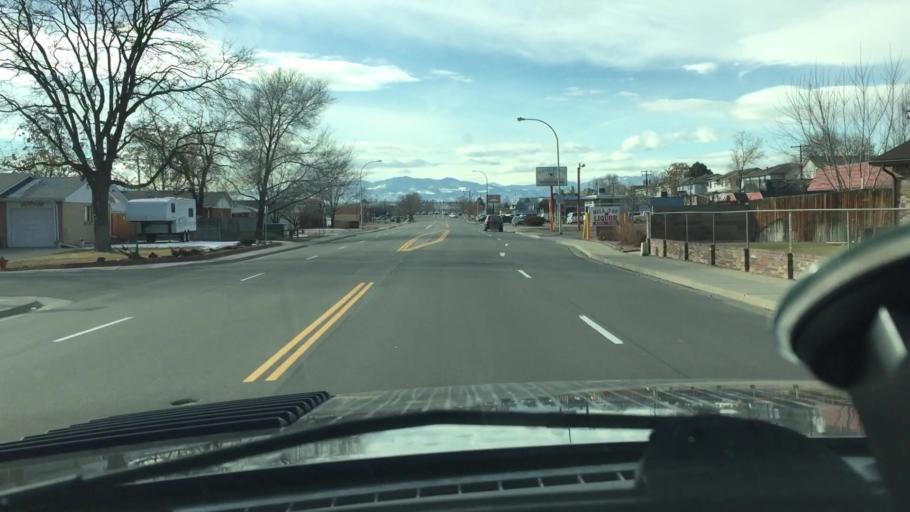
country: US
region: Colorado
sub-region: Adams County
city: Twin Lakes
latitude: 39.8273
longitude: -105.0193
